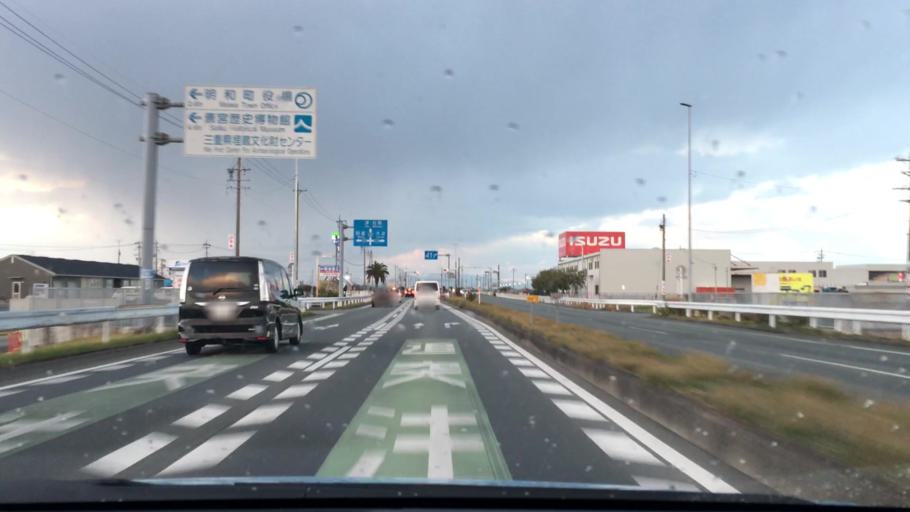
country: JP
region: Mie
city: Ise
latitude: 34.5552
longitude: 136.6517
